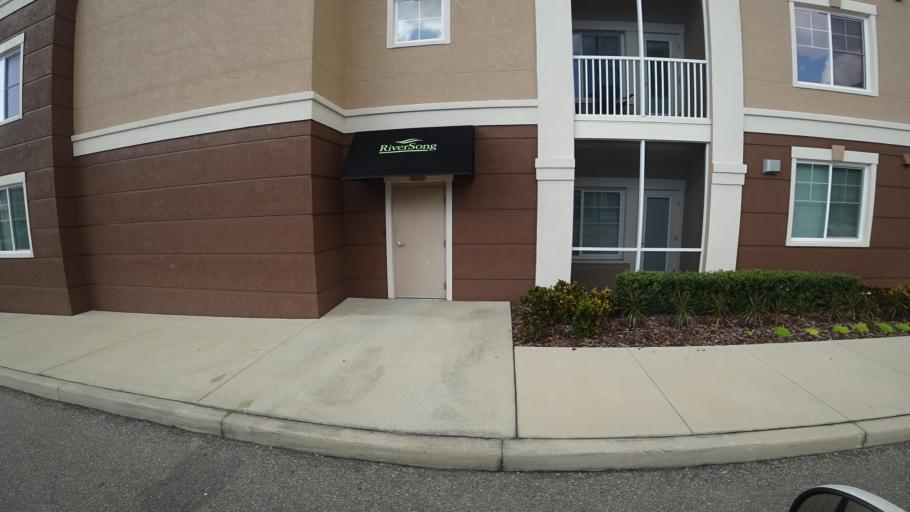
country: US
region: Florida
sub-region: Manatee County
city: Bradenton
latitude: 27.4987
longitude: -82.5687
